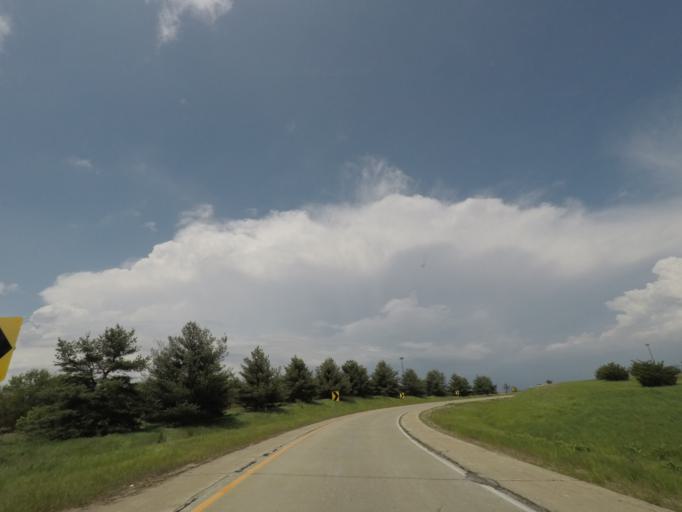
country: US
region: Illinois
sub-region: McLean County
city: Normal
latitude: 40.5368
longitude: -89.0094
